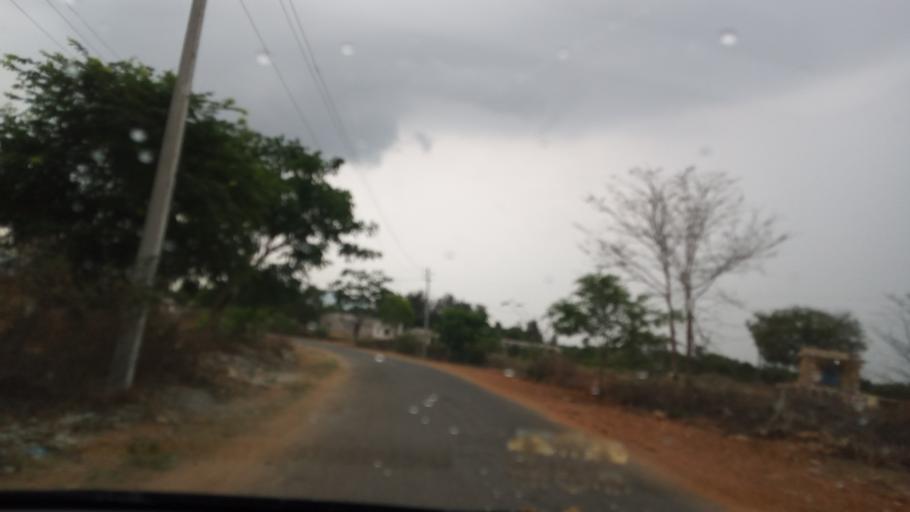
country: IN
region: Karnataka
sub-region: Kolar
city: Mulbagal
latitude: 13.1412
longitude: 78.3655
